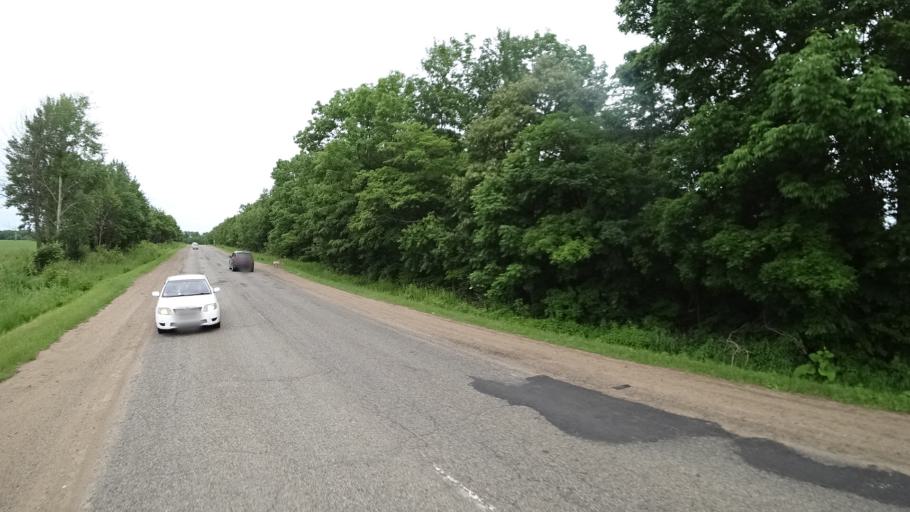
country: RU
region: Primorskiy
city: Novosysoyevka
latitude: 44.1845
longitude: 133.3520
